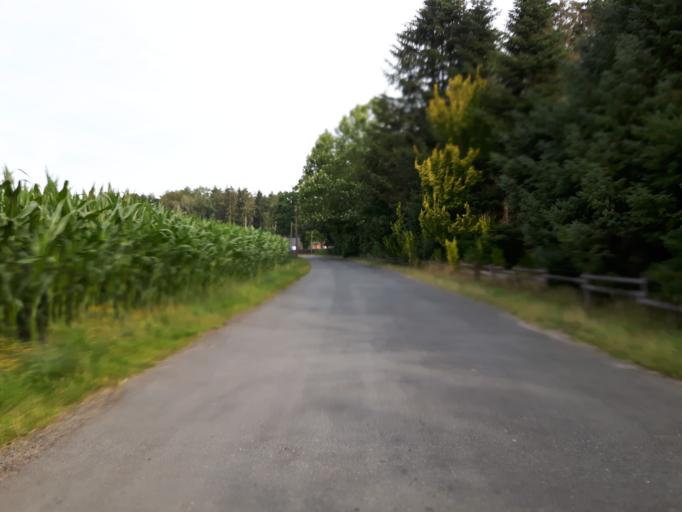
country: DE
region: Lower Saxony
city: Delmenhorst
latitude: 53.0809
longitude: 8.6428
